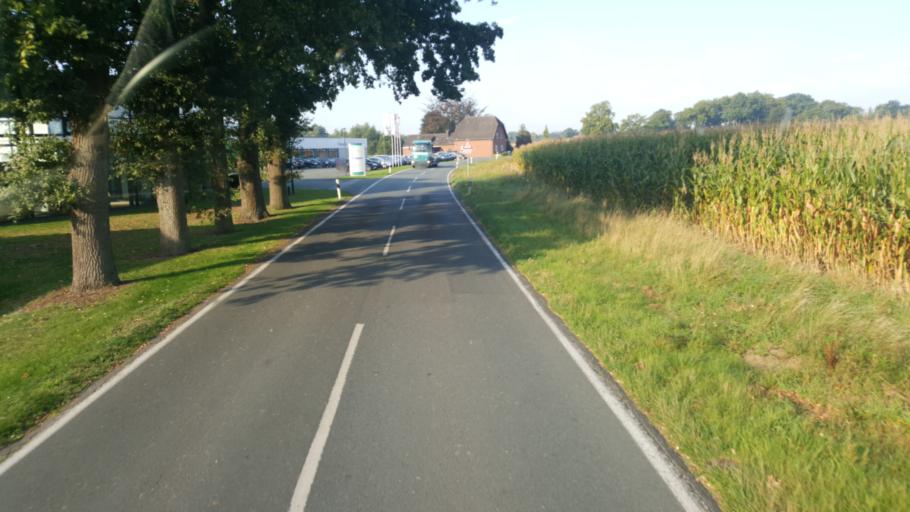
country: DE
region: North Rhine-Westphalia
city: Rietberg
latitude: 51.7384
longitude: 8.4051
